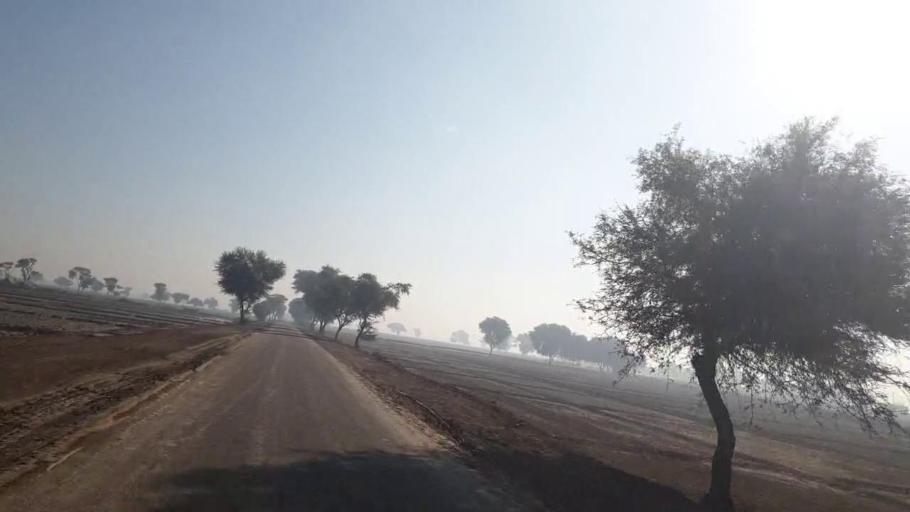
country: PK
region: Sindh
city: Dadu
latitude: 26.6728
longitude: 67.8203
